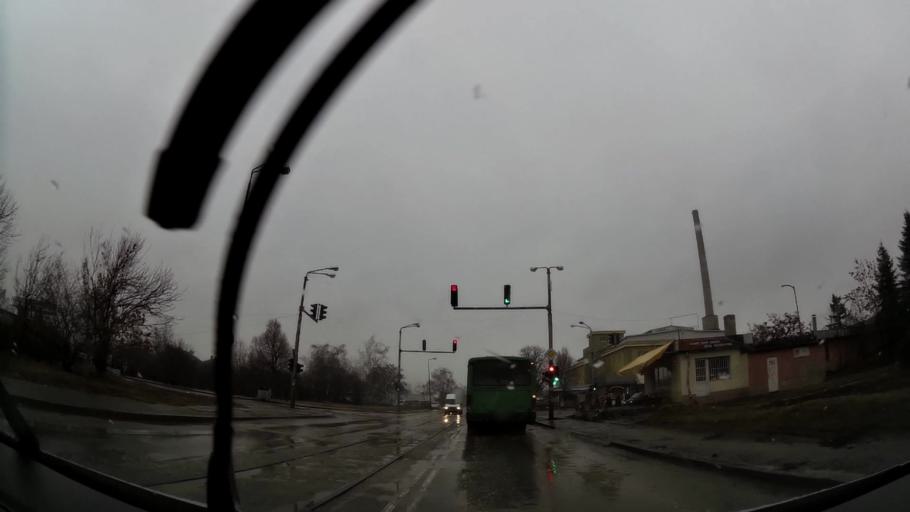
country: BG
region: Sofia-Capital
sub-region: Stolichna Obshtina
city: Sofia
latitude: 42.6629
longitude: 23.4153
